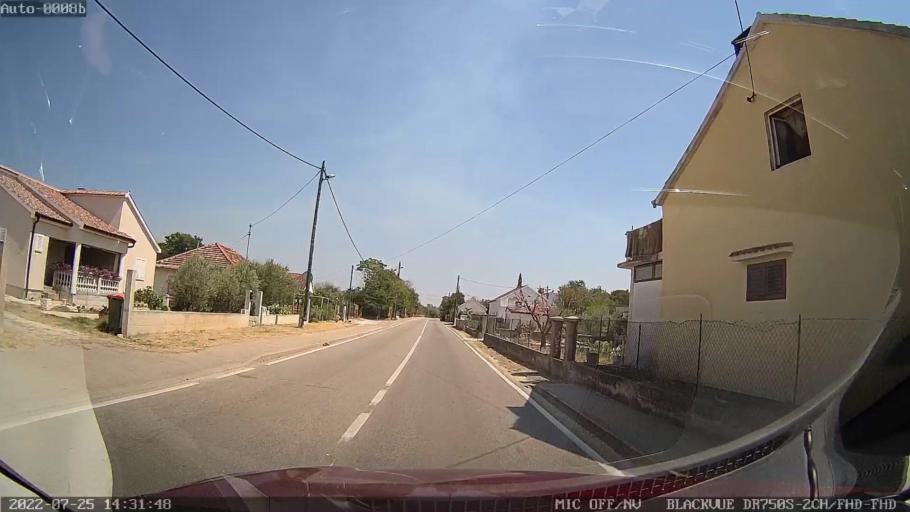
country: HR
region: Zadarska
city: Galovac
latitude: 44.1089
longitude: 15.3751
